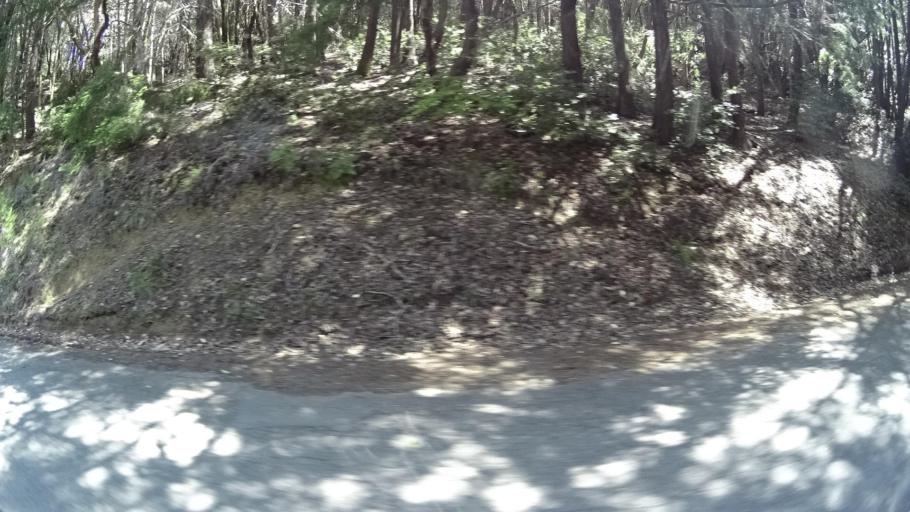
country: US
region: California
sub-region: Humboldt County
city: Redway
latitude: 40.1050
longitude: -123.9535
